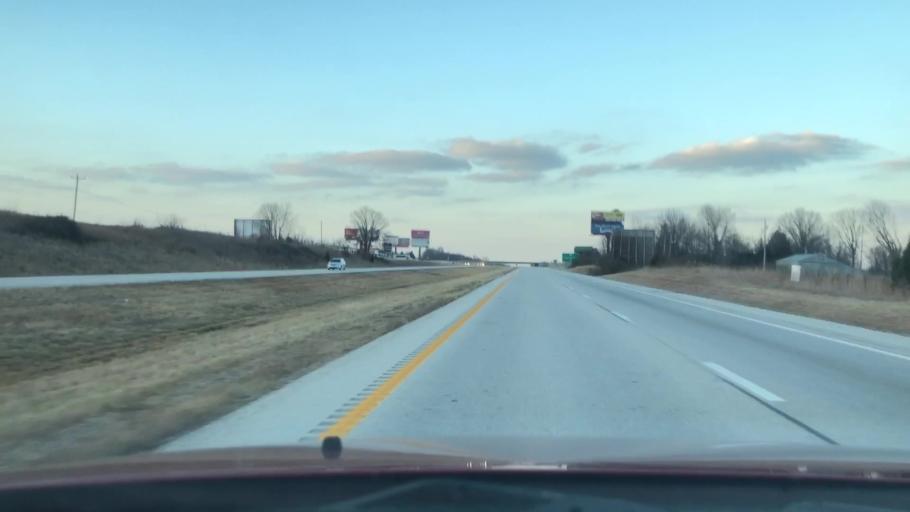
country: US
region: Missouri
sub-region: Christian County
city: Ozark
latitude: 36.9352
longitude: -93.2321
